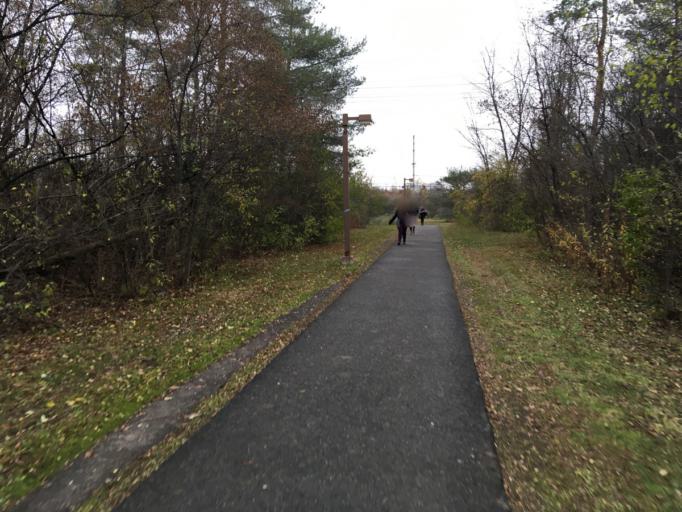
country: CA
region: Ontario
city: Ottawa
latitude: 45.4044
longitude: -75.6494
